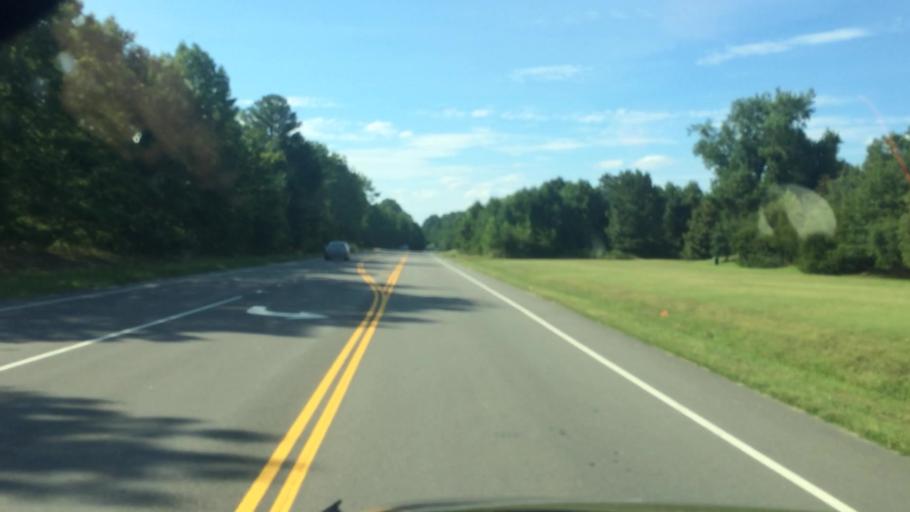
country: US
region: Virginia
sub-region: City of Williamsburg
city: Williamsburg
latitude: 37.2930
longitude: -76.7228
